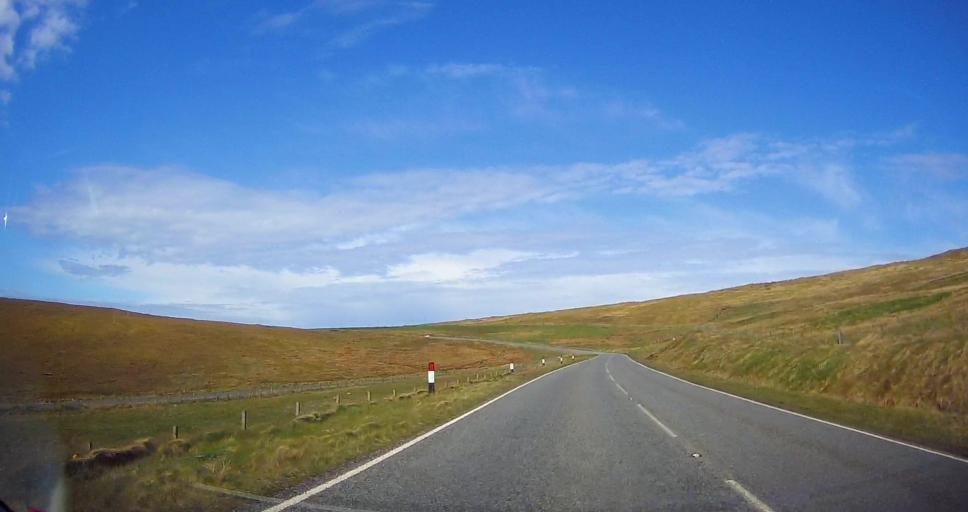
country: GB
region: Scotland
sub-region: Shetland Islands
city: Sandwick
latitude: 60.0093
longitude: -1.2530
